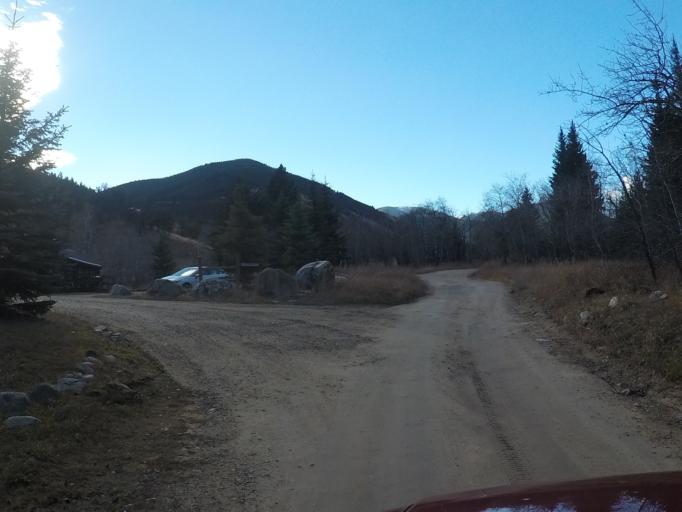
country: US
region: Montana
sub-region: Carbon County
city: Red Lodge
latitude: 45.1205
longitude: -109.2966
